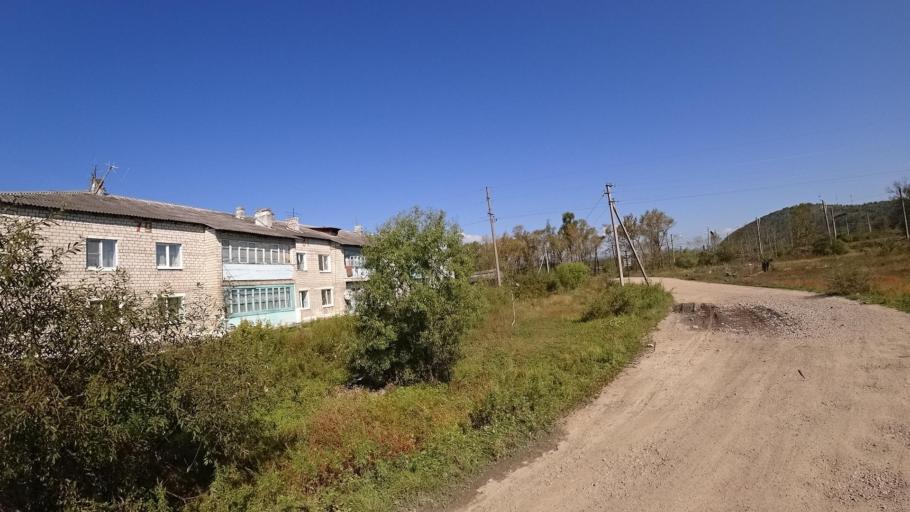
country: RU
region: Jewish Autonomous Oblast
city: Bira
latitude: 49.0009
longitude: 132.4509
